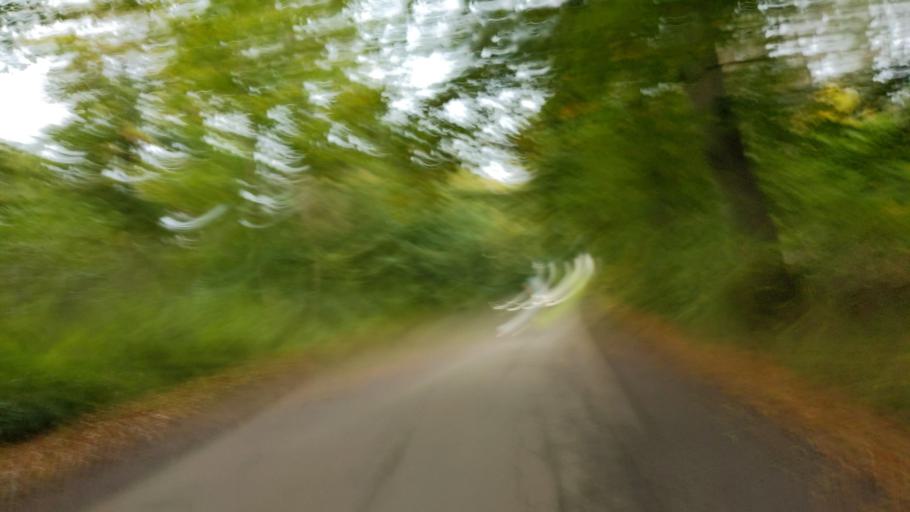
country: DE
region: Schleswig-Holstein
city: Altenkrempe
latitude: 54.1388
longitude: 10.8099
